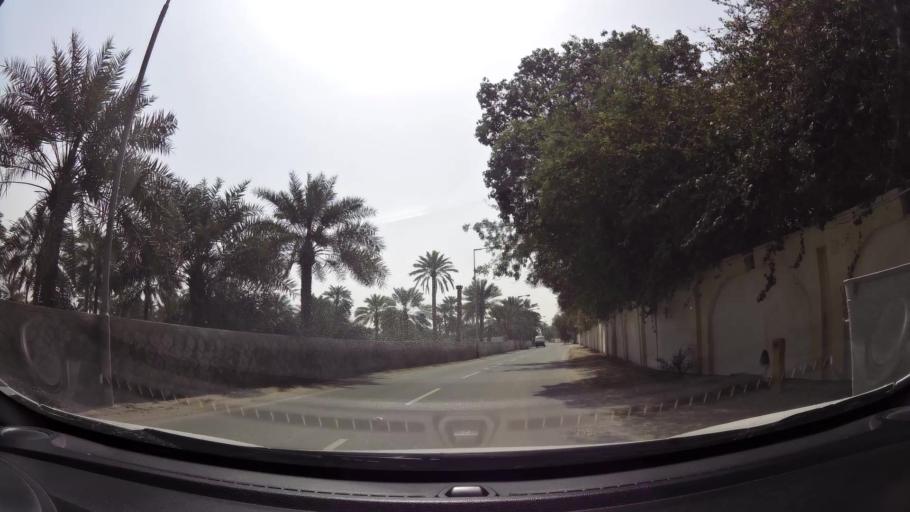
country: BH
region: Manama
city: Jidd Hafs
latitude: 26.2266
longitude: 50.5037
